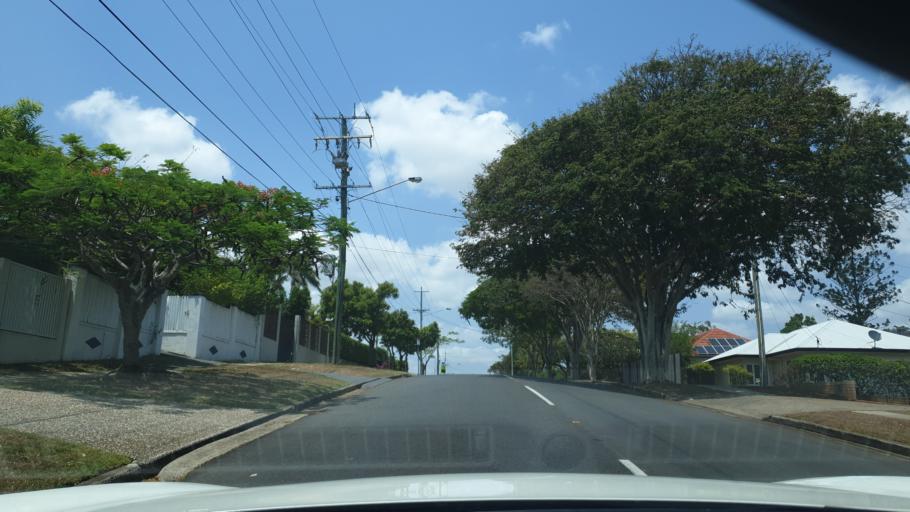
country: AU
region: Queensland
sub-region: Brisbane
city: Chermside West
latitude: -27.3662
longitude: 153.0262
